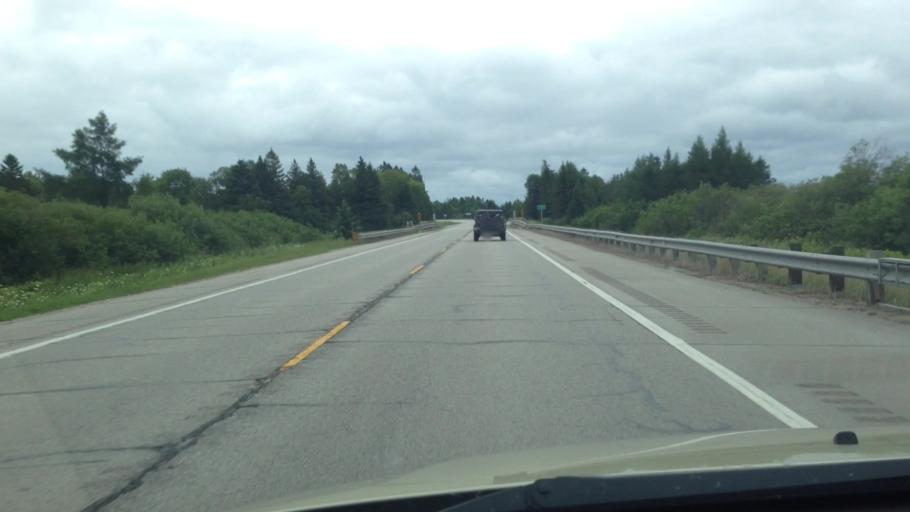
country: US
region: Michigan
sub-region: Luce County
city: Newberry
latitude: 46.0962
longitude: -85.4753
